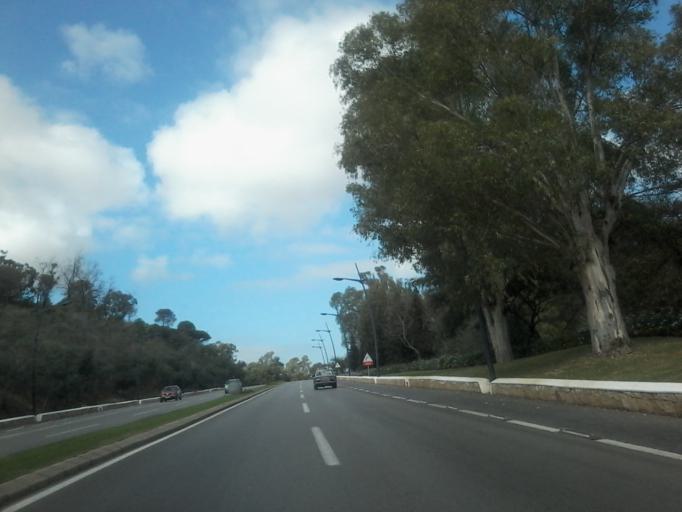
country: MA
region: Tanger-Tetouan
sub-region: Tetouan
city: Martil
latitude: 35.6707
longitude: -5.3208
